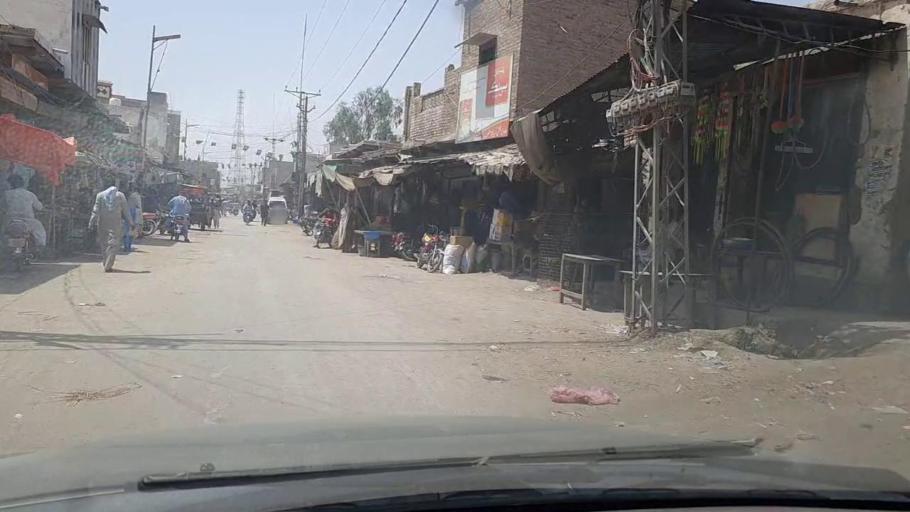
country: PK
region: Sindh
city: Miro Khan
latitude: 27.7614
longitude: 68.0933
